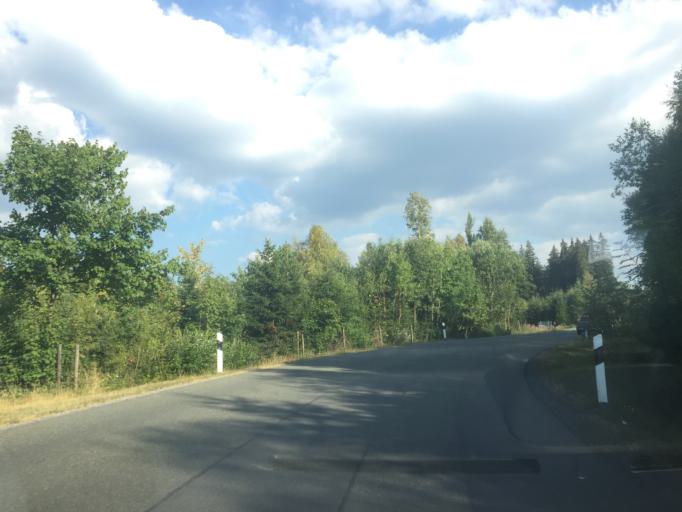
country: DE
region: Lower Saxony
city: Braunlage
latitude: 51.7148
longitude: 10.6224
